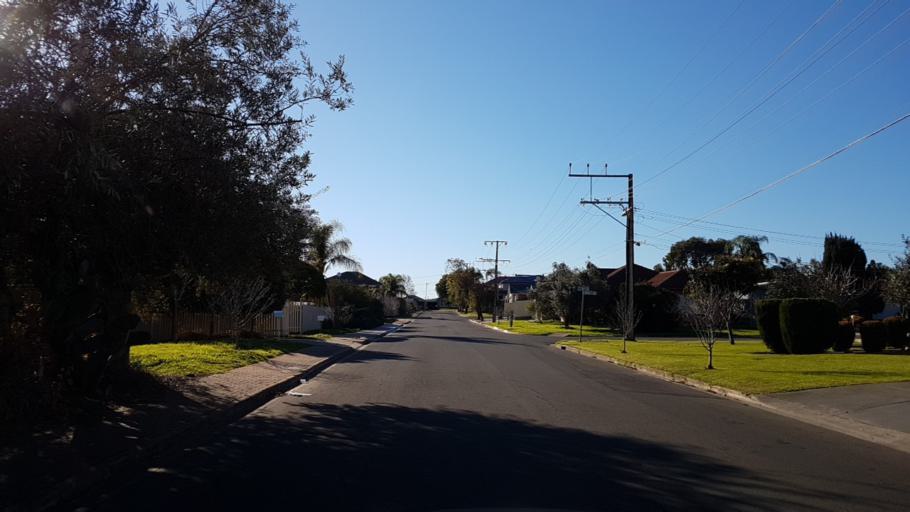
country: AU
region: South Australia
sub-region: Campbelltown
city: Paradise
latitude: -34.8810
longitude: 138.6814
